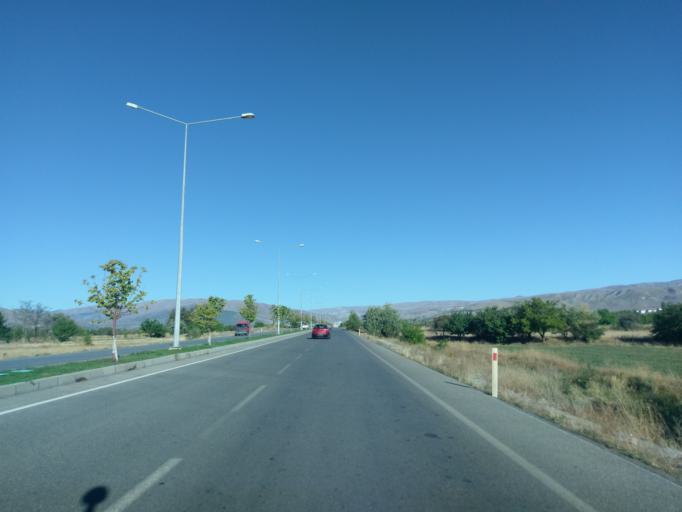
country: TR
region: Erzincan
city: Erzincan
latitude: 39.7809
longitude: 39.4088
